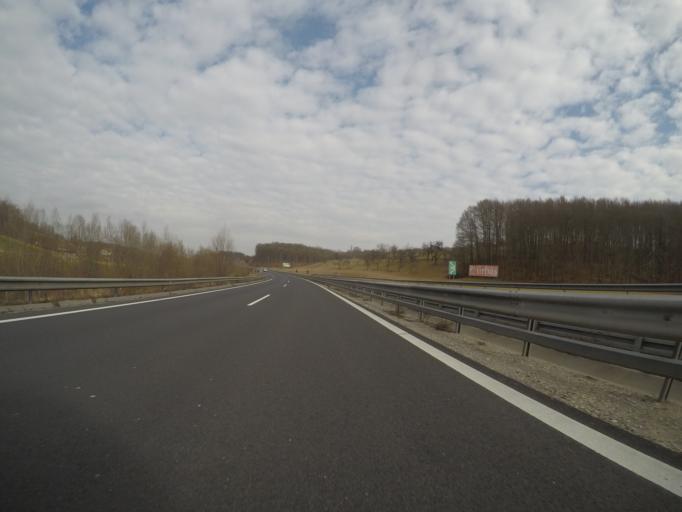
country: SI
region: Cerkvenjak
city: Cerkvenjak
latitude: 46.5803
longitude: 15.9640
